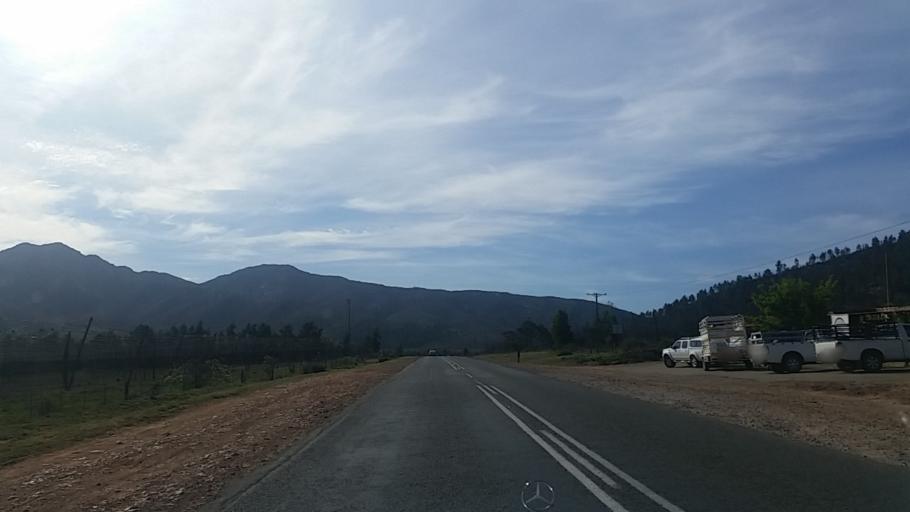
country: ZA
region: Western Cape
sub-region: Eden District Municipality
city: George
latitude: -33.8500
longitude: 22.3558
